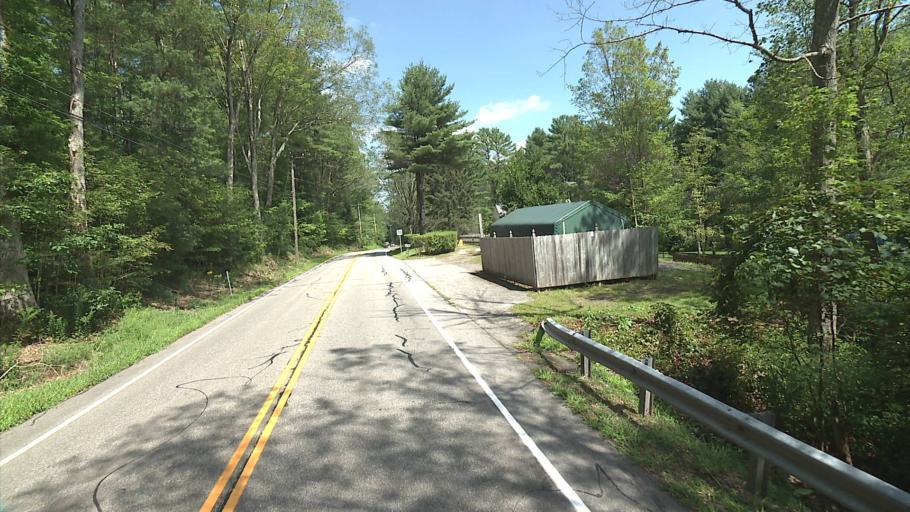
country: US
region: Connecticut
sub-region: Windham County
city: South Woodstock
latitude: 41.9137
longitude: -72.0777
